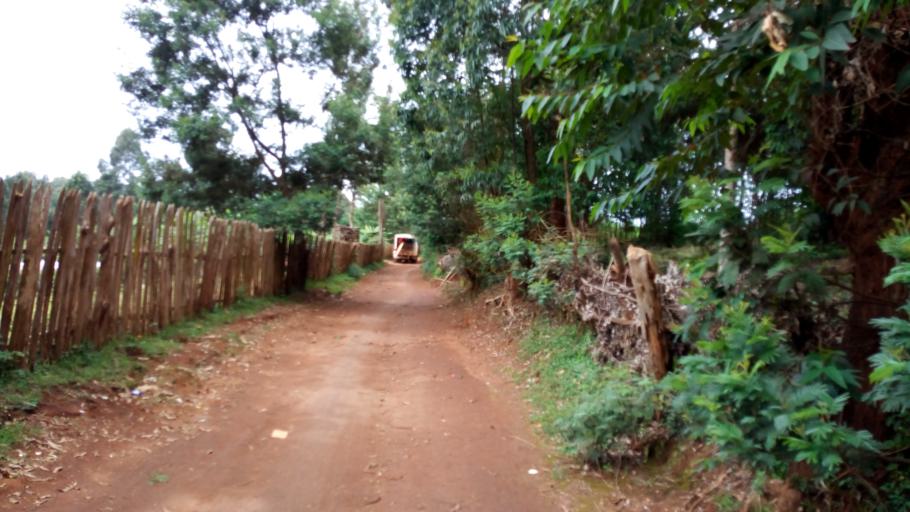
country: KE
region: Makueni
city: Wote
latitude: -1.6573
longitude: 37.4549
